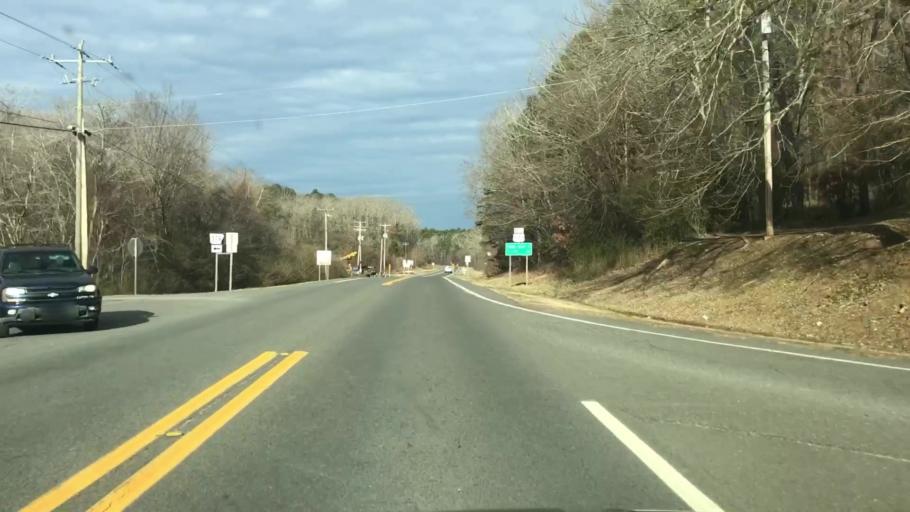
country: US
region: Arkansas
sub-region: Montgomery County
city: Mount Ida
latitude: 34.5625
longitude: -93.6401
